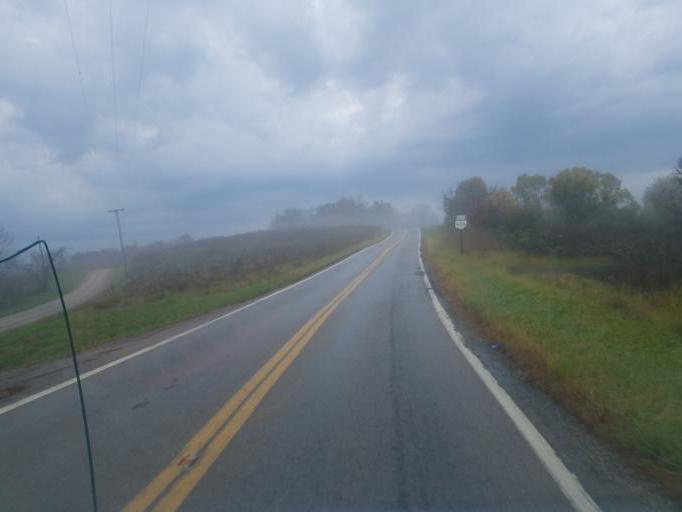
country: US
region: Ohio
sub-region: Morgan County
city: McConnelsville
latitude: 39.4958
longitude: -81.8920
